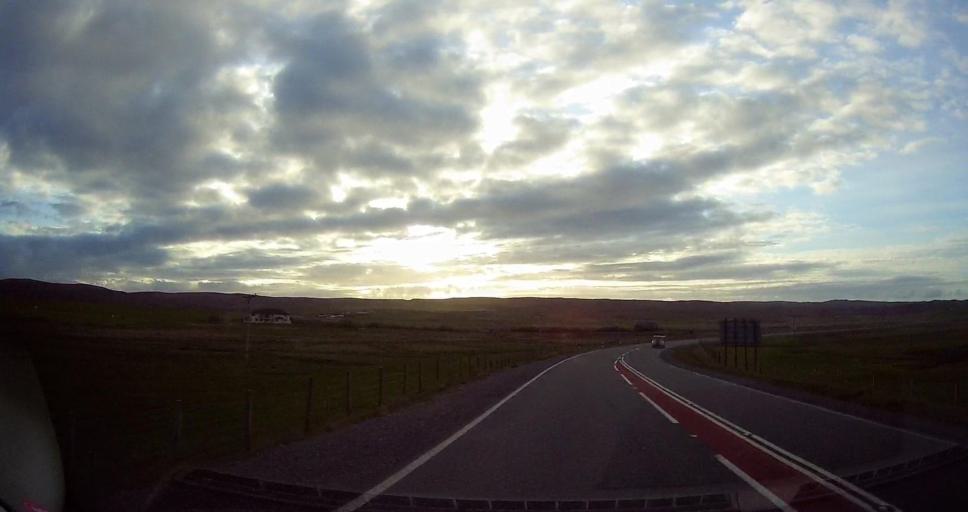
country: GB
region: Scotland
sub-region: Shetland Islands
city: Lerwick
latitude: 60.1872
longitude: -1.2288
